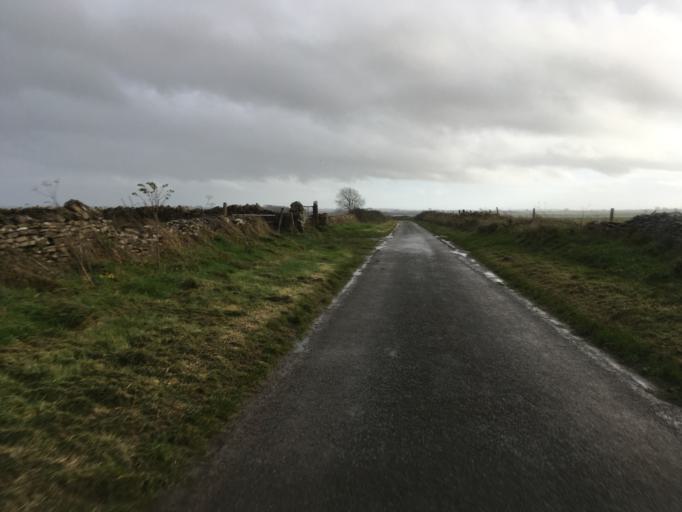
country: GB
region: England
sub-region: South Gloucestershire
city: Cold Ashton
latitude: 51.4705
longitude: -2.3624
